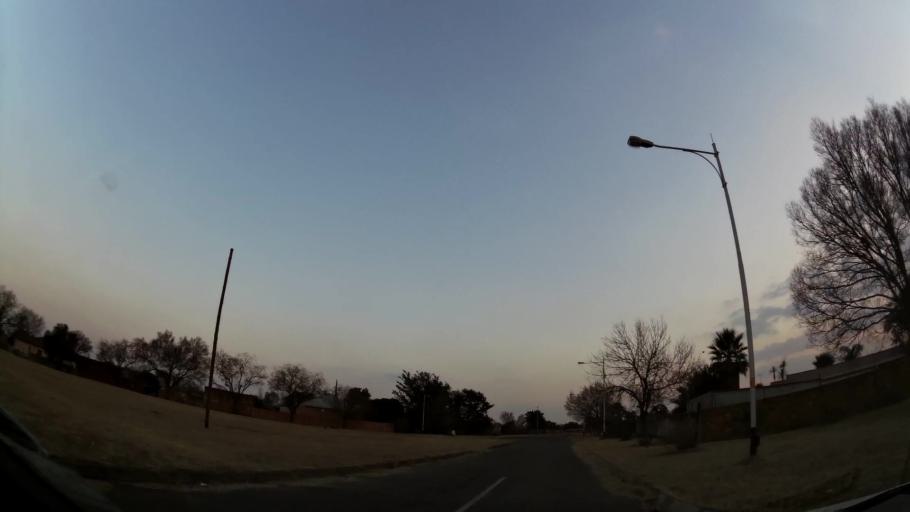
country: ZA
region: Gauteng
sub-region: Ekurhuleni Metropolitan Municipality
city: Nigel
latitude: -26.3527
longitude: 28.4362
